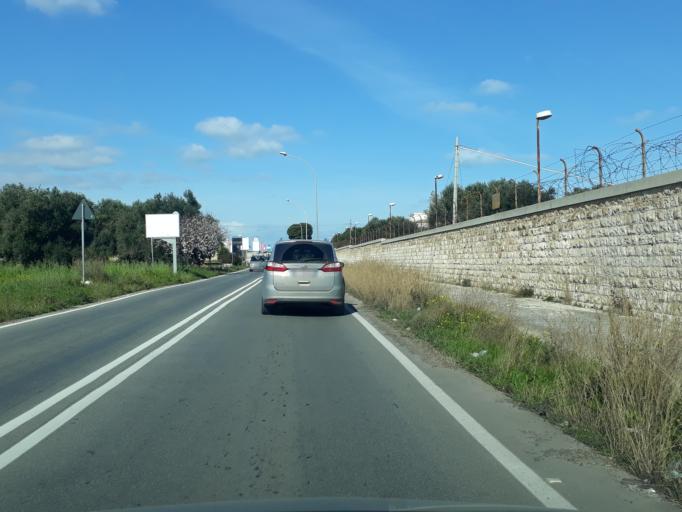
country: IT
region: Apulia
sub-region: Provincia di Bari
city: Monopoli
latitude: 40.9529
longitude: 17.2852
